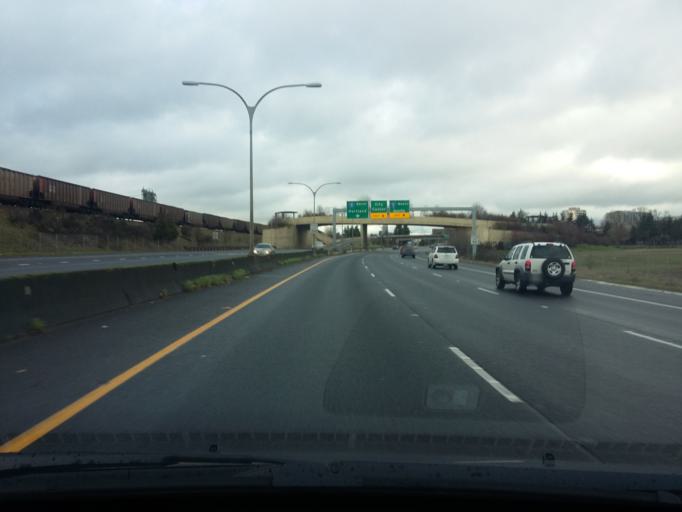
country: US
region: Washington
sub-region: Clark County
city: Vancouver
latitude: 45.6200
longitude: -122.6646
